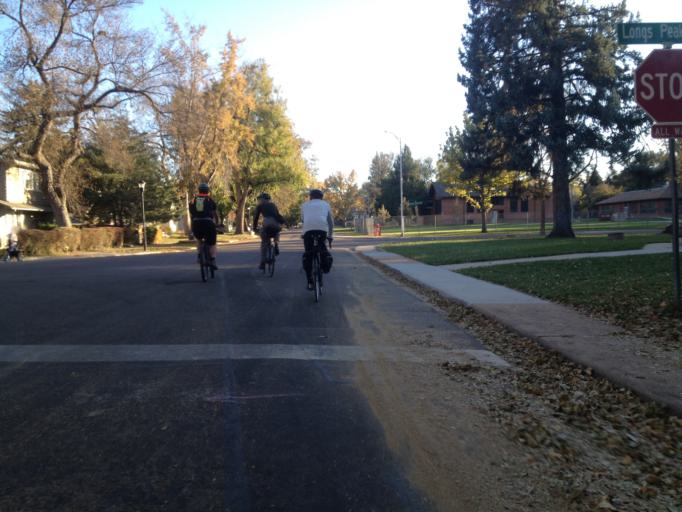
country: US
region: Colorado
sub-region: Boulder County
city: Longmont
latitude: 40.1708
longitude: -105.1119
